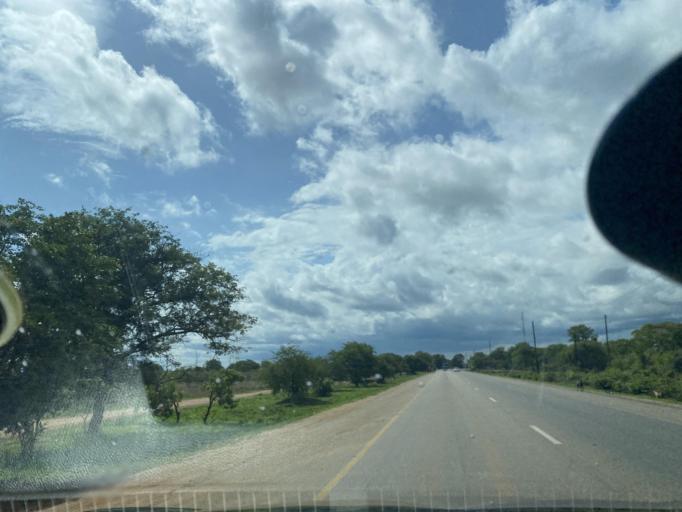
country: ZM
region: Lusaka
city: Kafue
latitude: -15.8549
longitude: 28.2556
